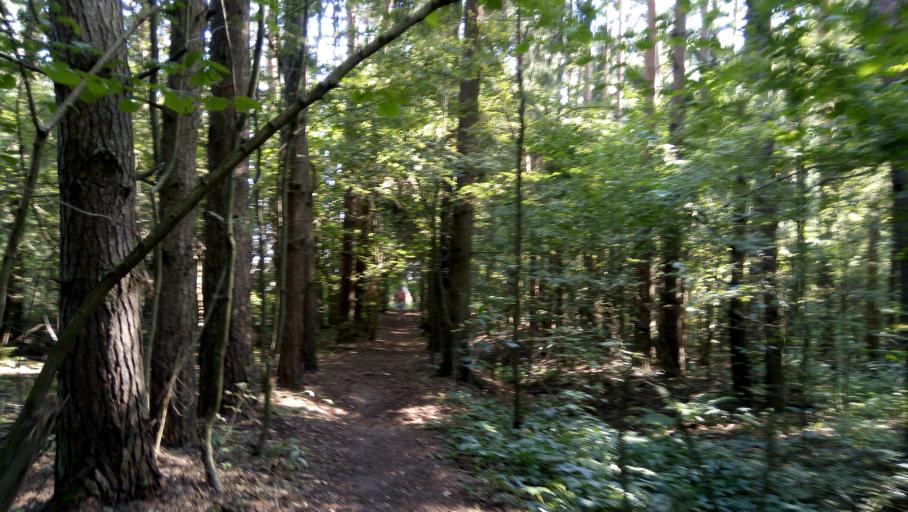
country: RU
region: Moskovskaya
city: Proletarskiy
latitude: 55.0526
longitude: 37.4009
